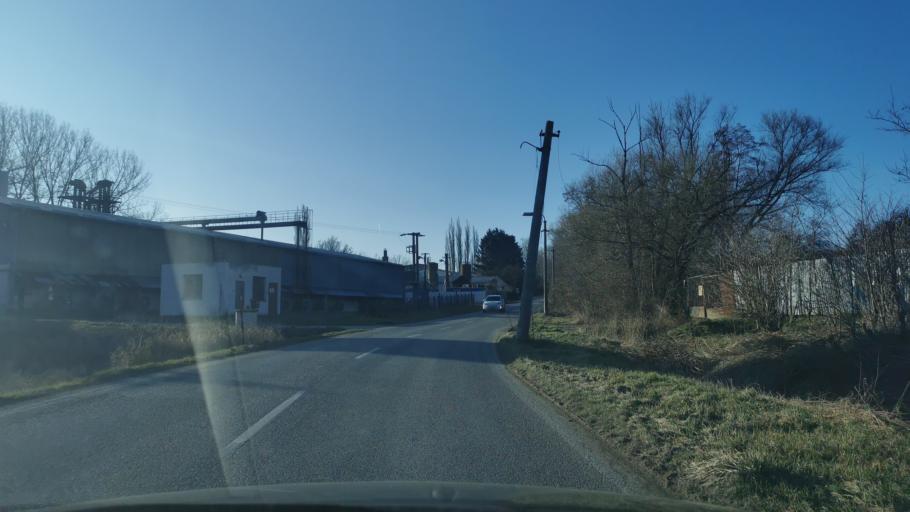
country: SK
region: Trnavsky
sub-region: Okres Senica
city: Senica
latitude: 48.7317
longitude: 17.3951
